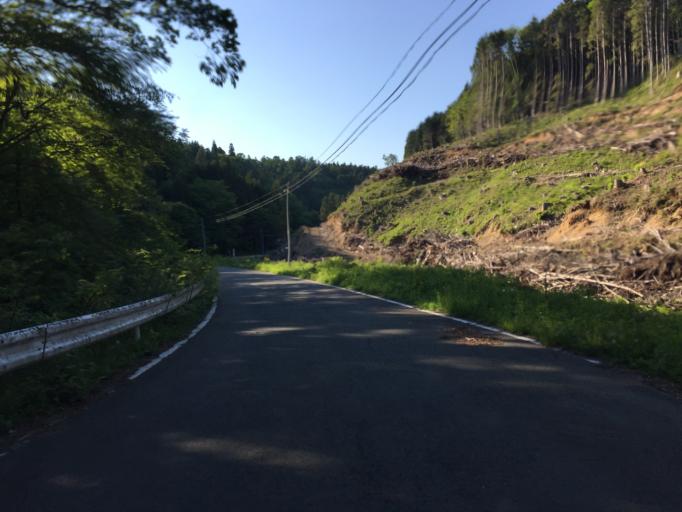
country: JP
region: Ibaraki
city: Kitaibaraki
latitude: 36.8985
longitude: 140.5952
